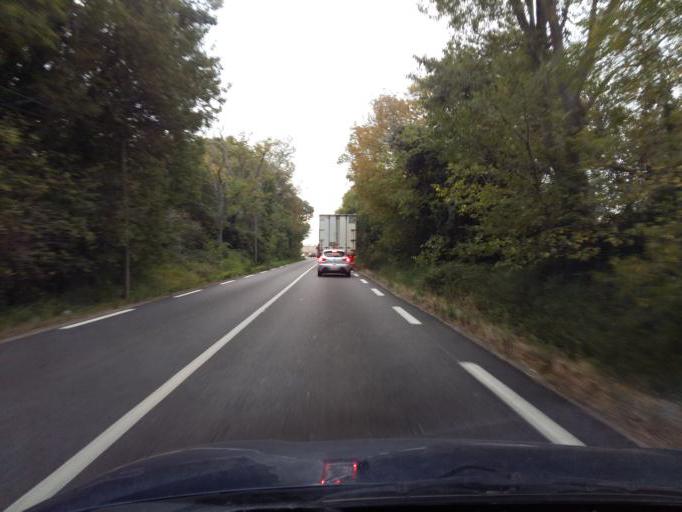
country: FR
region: Provence-Alpes-Cote d'Azur
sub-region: Departement des Bouches-du-Rhone
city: Miramas
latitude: 43.6108
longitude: 5.0108
